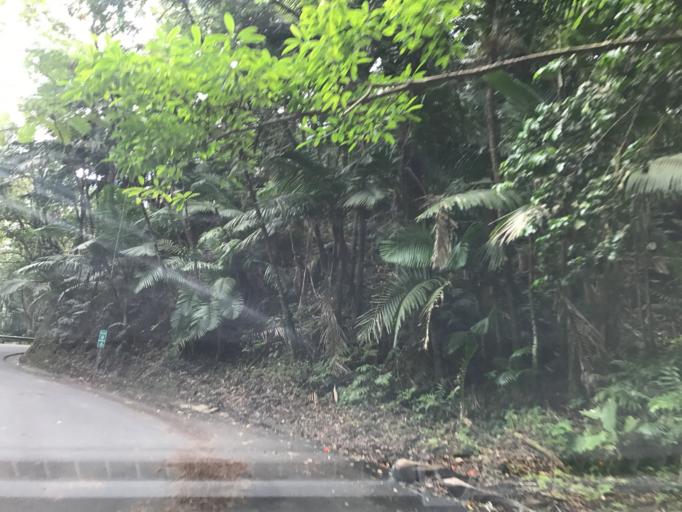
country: PR
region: Rio Grande
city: Palmer
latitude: 18.3172
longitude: -65.7713
